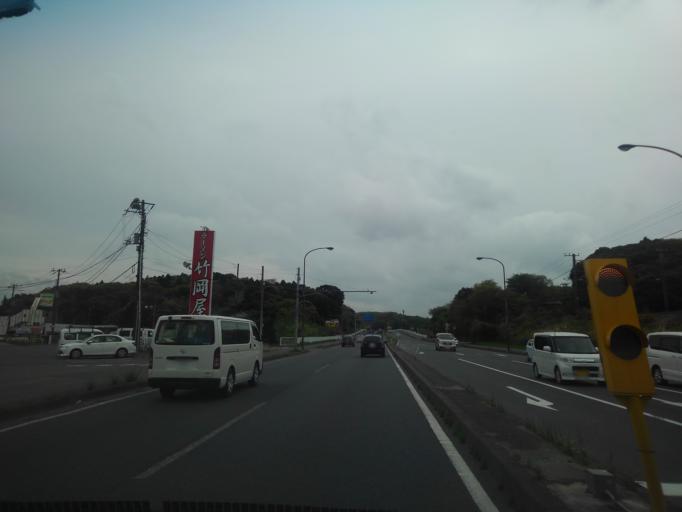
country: JP
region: Chiba
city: Kisarazu
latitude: 35.3572
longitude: 139.9209
